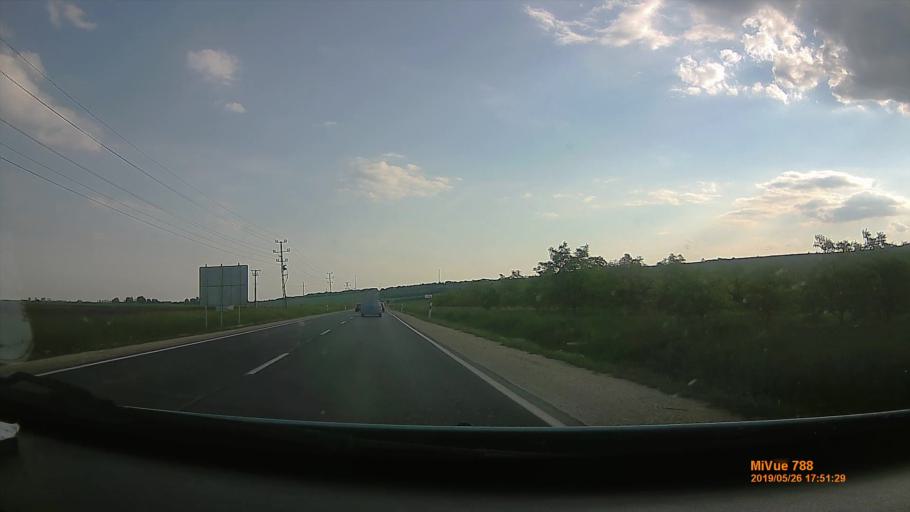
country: HU
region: Borsod-Abauj-Zemplen
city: Szikszo
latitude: 48.1743
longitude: 20.9140
